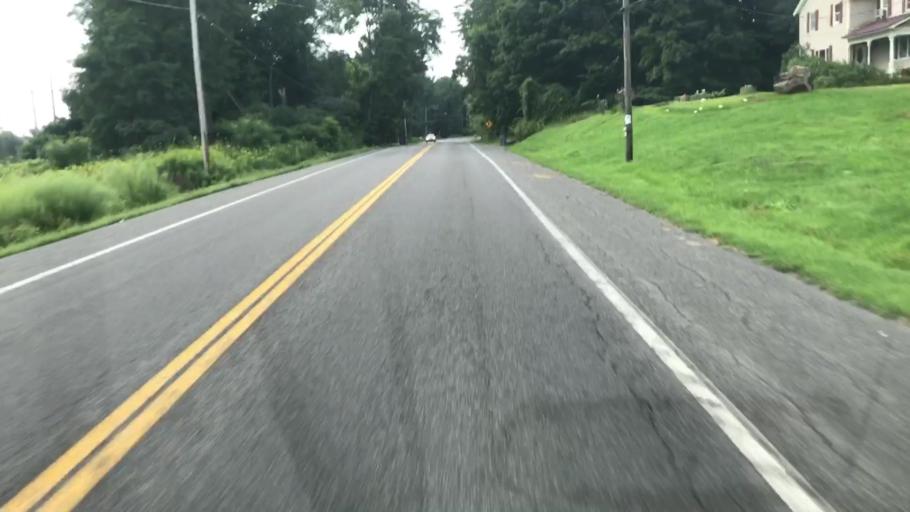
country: US
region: New York
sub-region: Onondaga County
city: Liverpool
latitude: 43.1666
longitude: -76.1956
